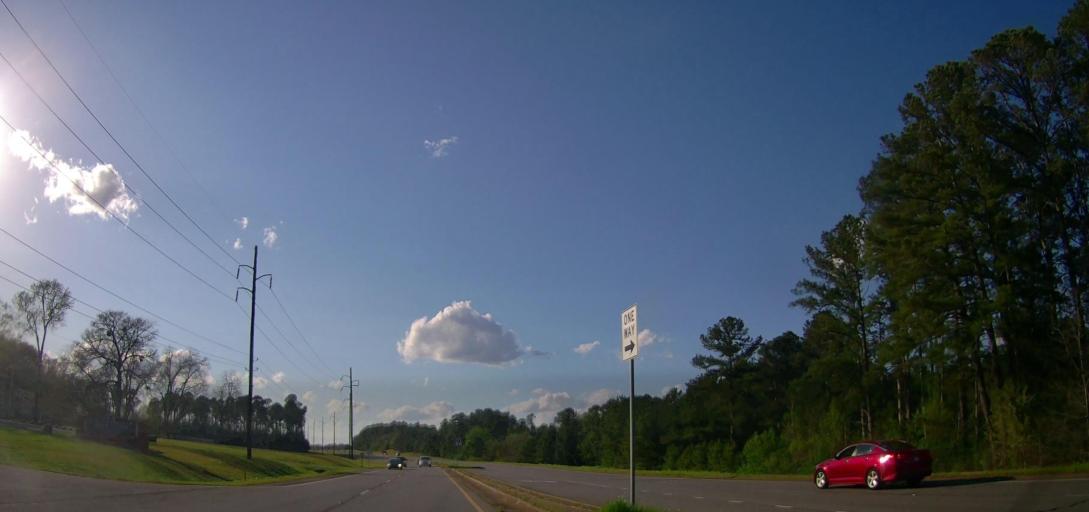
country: US
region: Georgia
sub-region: Baldwin County
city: Milledgeville
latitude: 33.0917
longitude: -83.2518
